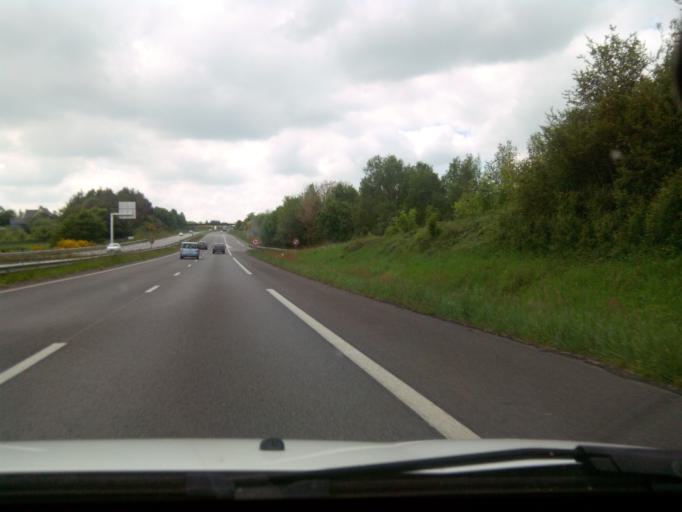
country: FR
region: Brittany
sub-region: Departement des Cotes-d'Armor
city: Plenee-Jugon
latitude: 48.3766
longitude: -2.3615
